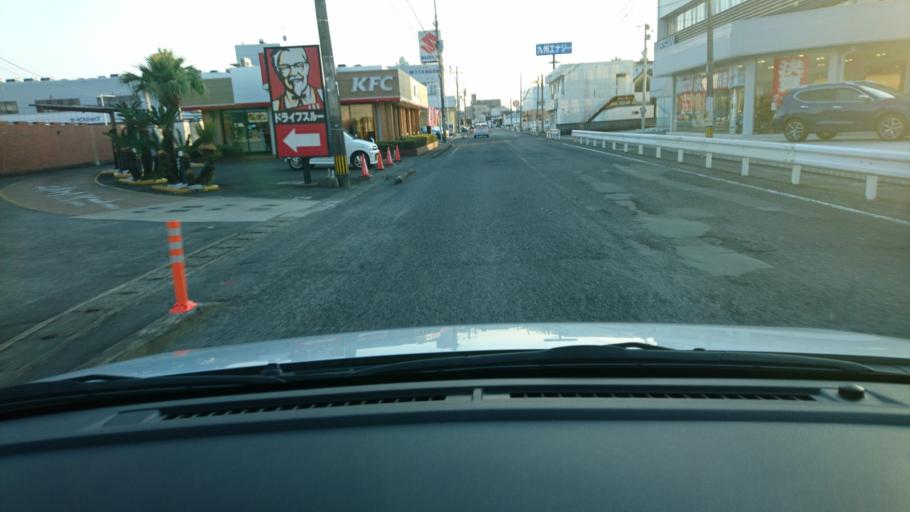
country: JP
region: Miyazaki
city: Miyazaki-shi
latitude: 31.9510
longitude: 131.4334
